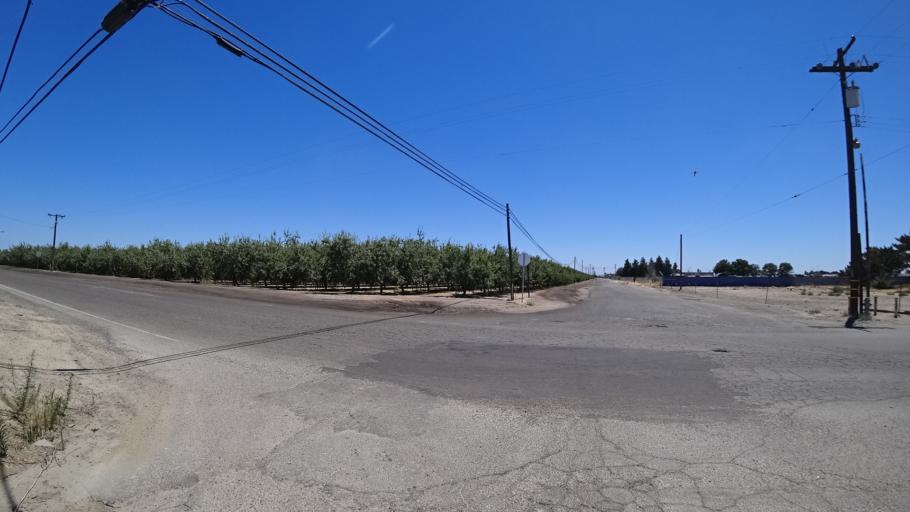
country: US
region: California
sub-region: Fresno County
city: Easton
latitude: 36.6707
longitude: -119.7458
